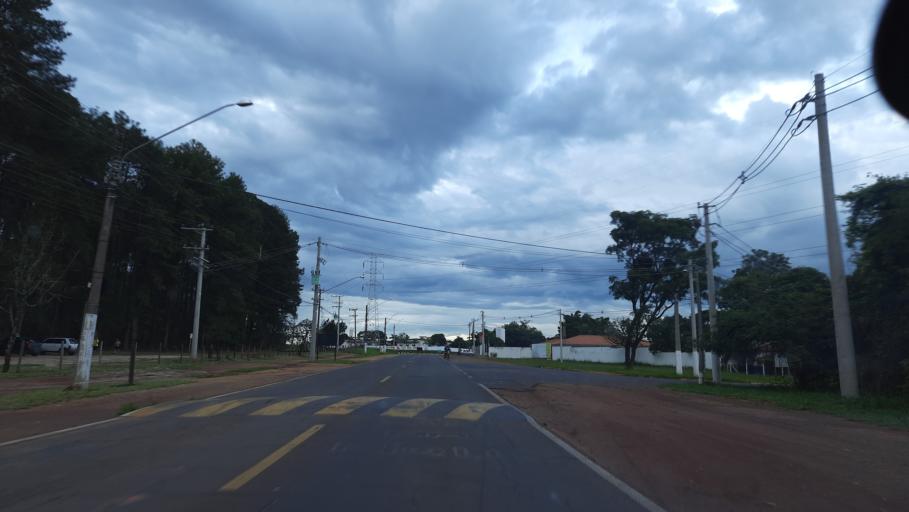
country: BR
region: Sao Paulo
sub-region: Casa Branca
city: Casa Branca
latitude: -21.7717
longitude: -47.0686
